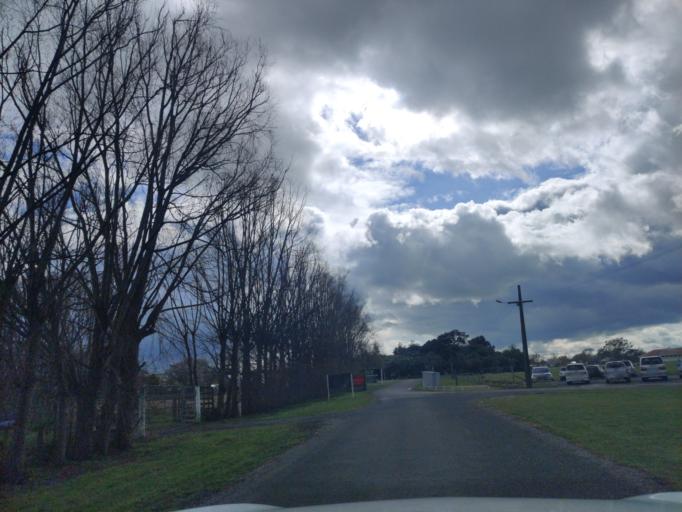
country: NZ
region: Manawatu-Wanganui
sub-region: Palmerston North City
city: Palmerston North
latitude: -40.2345
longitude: 175.5573
